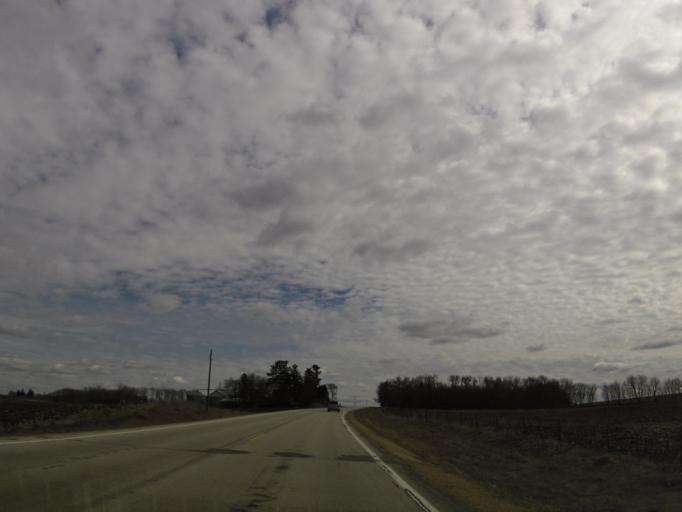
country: US
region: Minnesota
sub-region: Olmsted County
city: Stewartville
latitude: 43.8798
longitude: -92.4053
